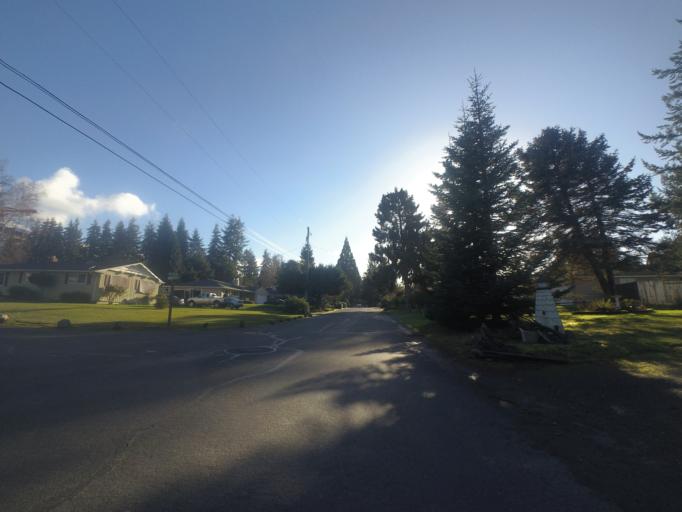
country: US
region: Washington
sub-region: Pierce County
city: University Place
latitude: 47.2271
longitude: -122.5403
